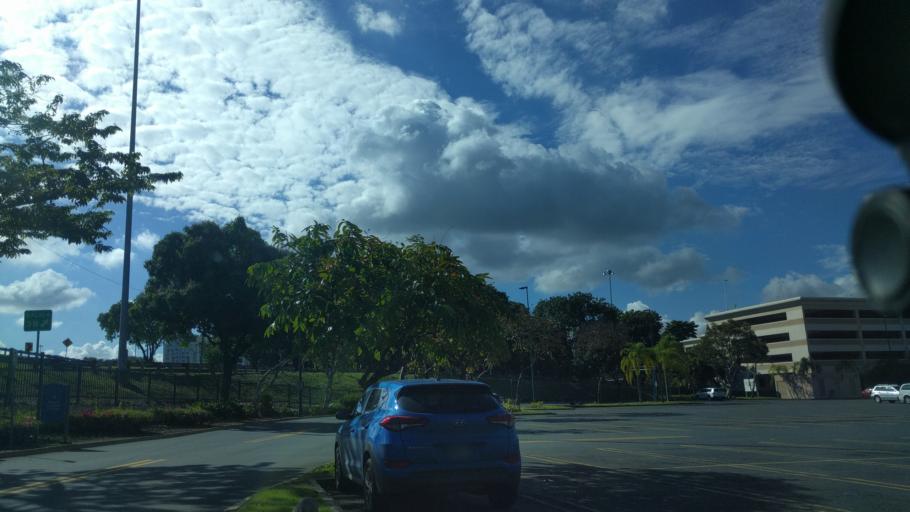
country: PR
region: Catano
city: Catano
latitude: 18.4218
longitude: -66.0720
